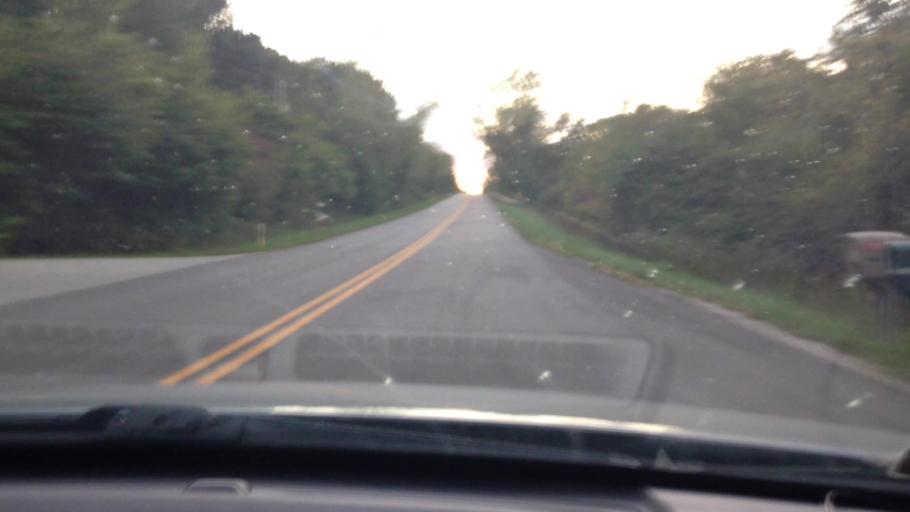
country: US
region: Kansas
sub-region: Leavenworth County
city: Lansing
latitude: 39.1867
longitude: -94.8712
